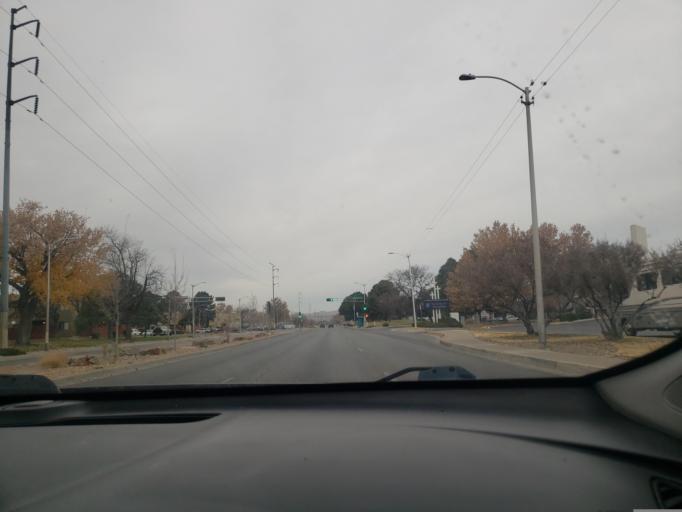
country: US
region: New Mexico
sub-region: Bernalillo County
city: North Valley
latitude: 35.1310
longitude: -106.5921
